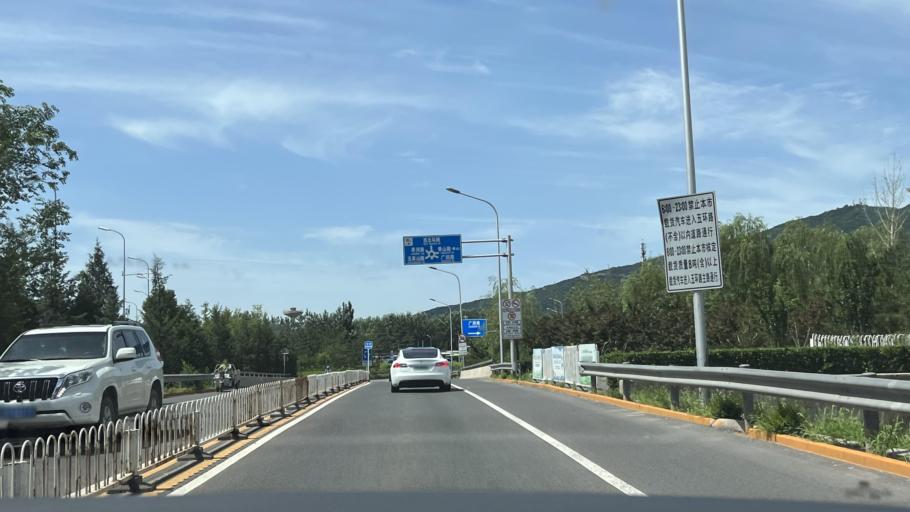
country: CN
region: Beijing
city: Xiangshan
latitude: 39.9931
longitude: 116.2170
